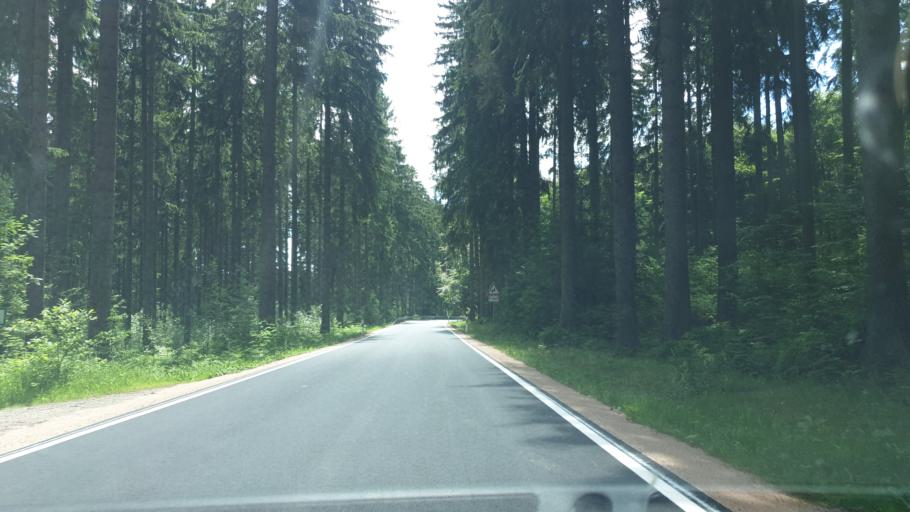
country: DE
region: Saxony
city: Breitenbrunn
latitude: 50.5132
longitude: 12.7426
